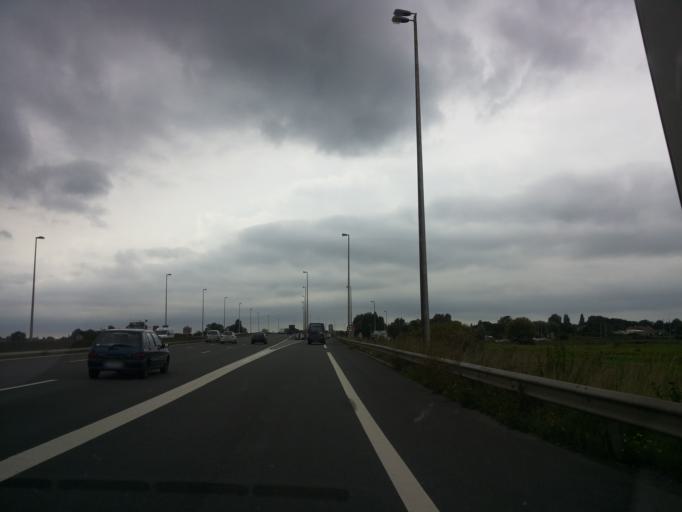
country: FR
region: Nord-Pas-de-Calais
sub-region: Departement du Pas-de-Calais
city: Coulogne
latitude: 50.9349
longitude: 1.8954
